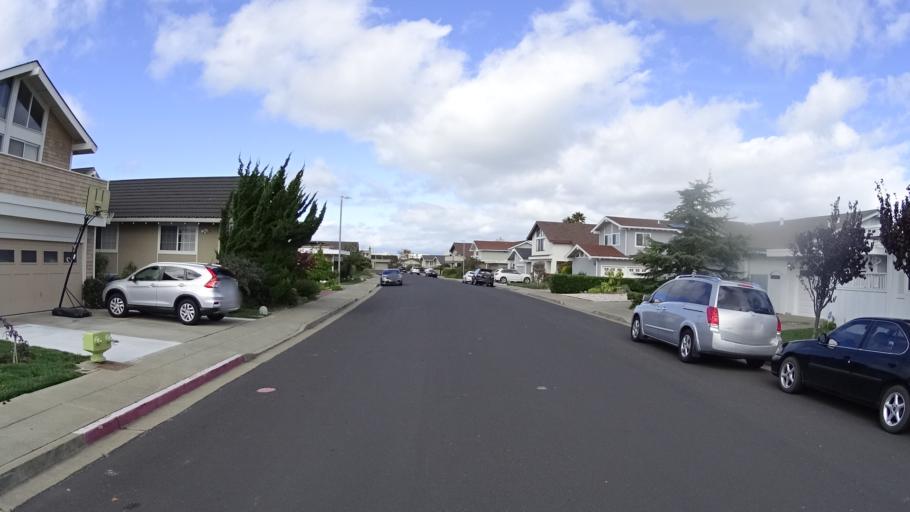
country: US
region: California
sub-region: San Mateo County
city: Foster City
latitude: 37.5623
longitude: -122.2579
